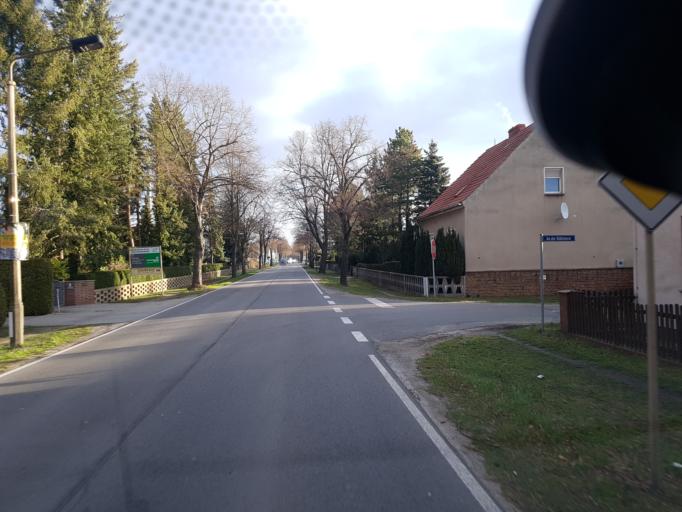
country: DE
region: Brandenburg
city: Luebben
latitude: 51.9465
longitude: 13.9166
